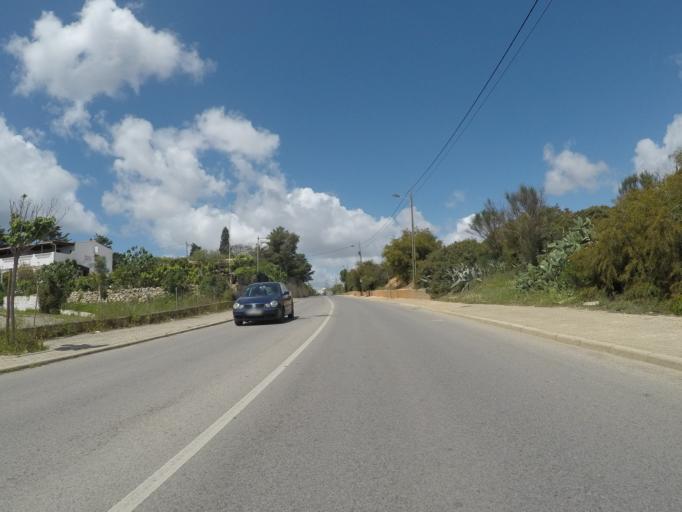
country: PT
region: Faro
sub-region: Silves
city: Armacao de Pera
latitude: 37.1048
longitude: -8.3761
